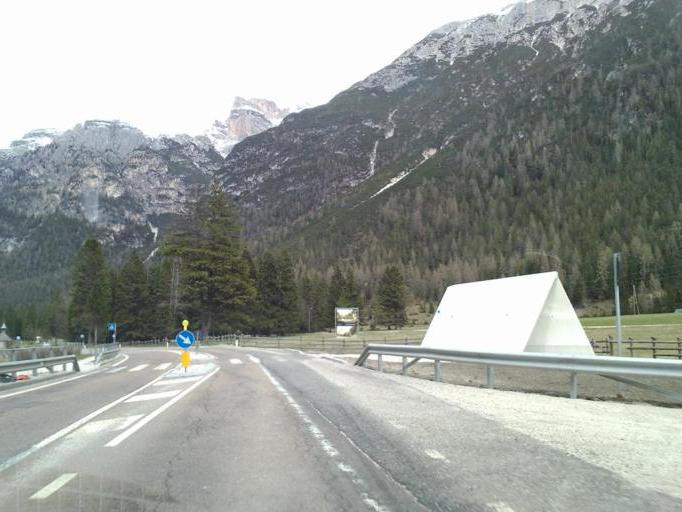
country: IT
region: Trentino-Alto Adige
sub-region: Bolzano
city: Dobbiaco
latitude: 46.6403
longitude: 12.2313
